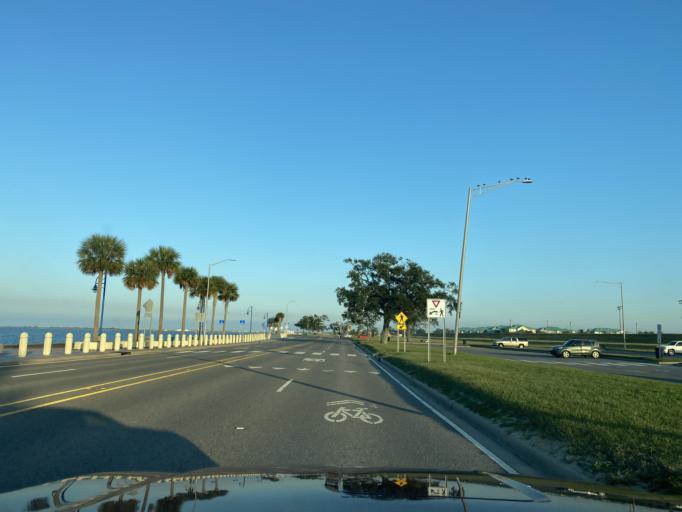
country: US
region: Louisiana
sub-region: Orleans Parish
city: New Orleans
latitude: 30.0347
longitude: -90.0503
